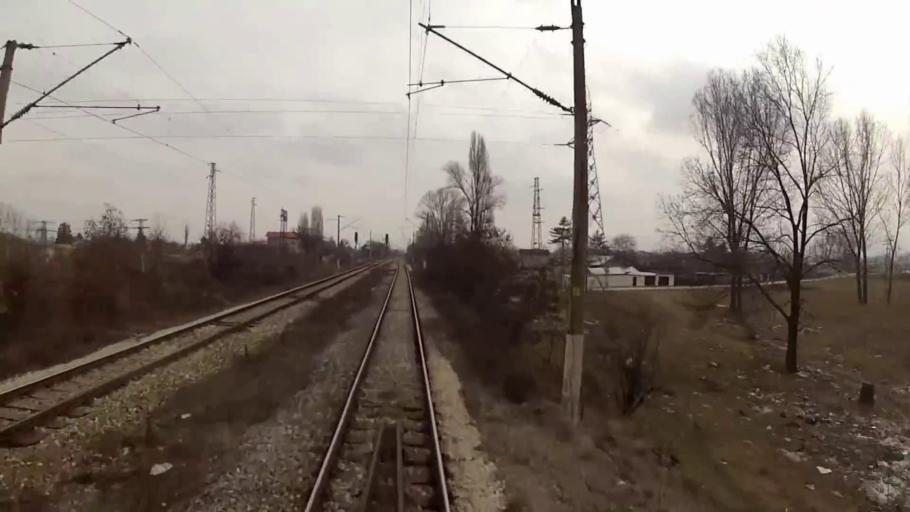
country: BG
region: Sofiya
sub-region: Obshtina Elin Pelin
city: Elin Pelin
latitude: 42.6528
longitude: 23.4672
